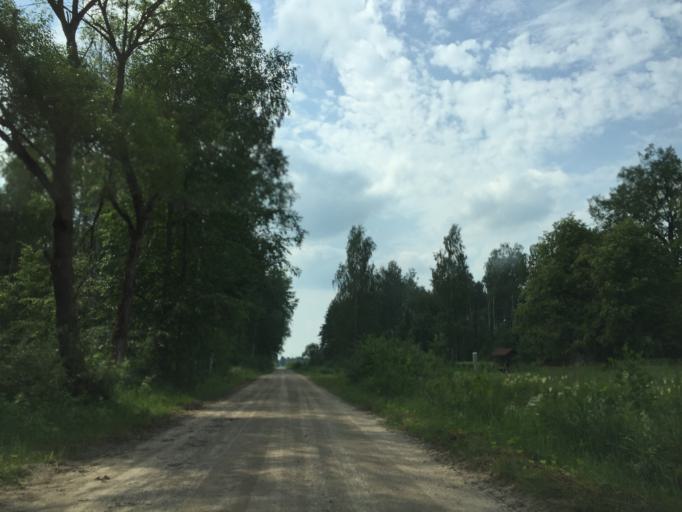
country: LV
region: Ozolnieku
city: Ozolnieki
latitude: 56.7537
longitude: 23.7420
